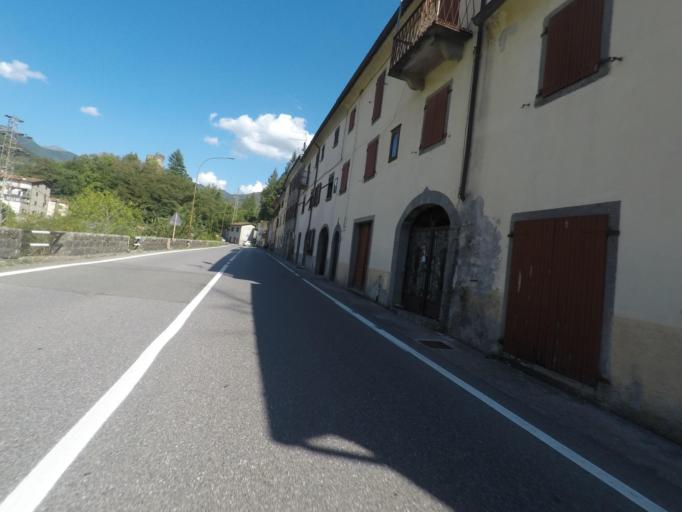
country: IT
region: Tuscany
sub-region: Provincia di Massa-Carrara
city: Fivizzano
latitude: 44.2421
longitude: 10.1360
